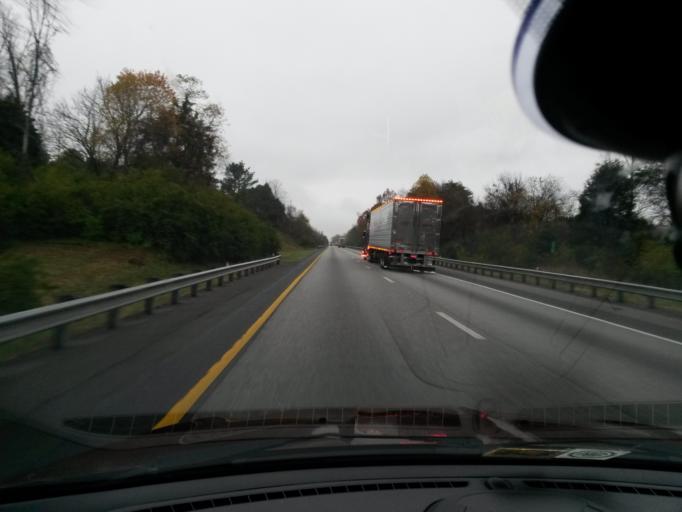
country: US
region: Virginia
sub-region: Botetourt County
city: Daleville
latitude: 37.4091
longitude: -79.8915
